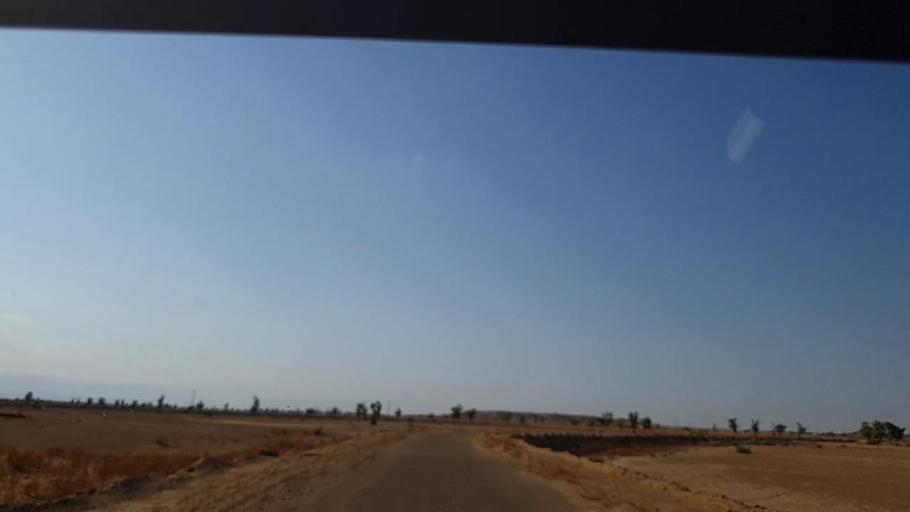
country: PK
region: Sindh
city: Johi
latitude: 26.5316
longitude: 67.5078
